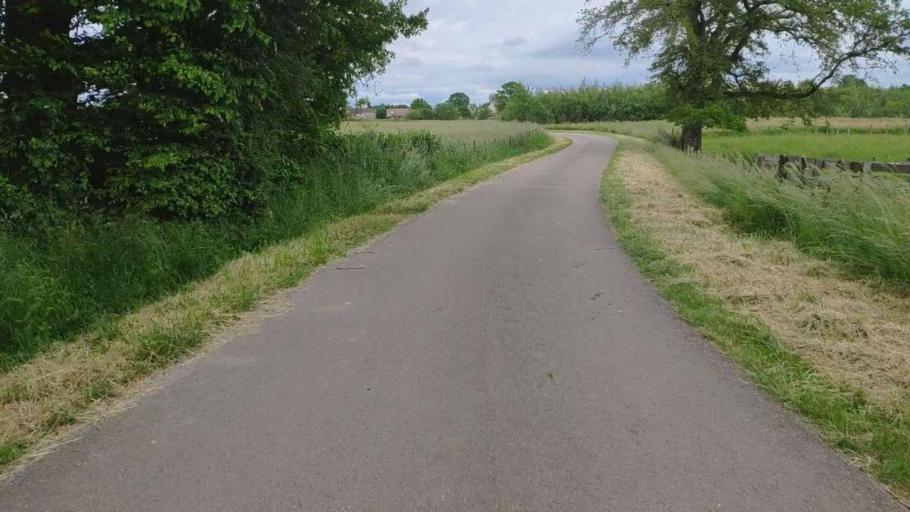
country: FR
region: Franche-Comte
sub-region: Departement du Jura
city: Bletterans
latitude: 46.7888
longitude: 5.5041
